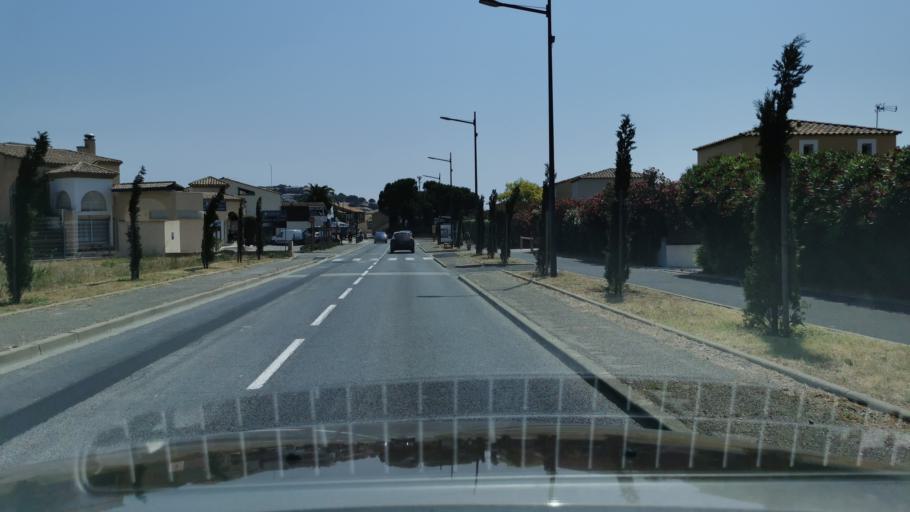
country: FR
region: Languedoc-Roussillon
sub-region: Departement de l'Aude
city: Leucate
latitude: 42.9065
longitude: 3.0349
